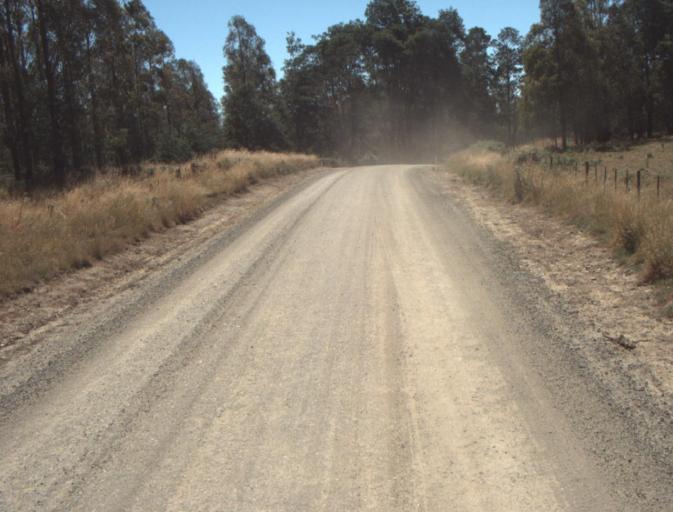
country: AU
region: Tasmania
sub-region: Dorset
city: Scottsdale
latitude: -41.3346
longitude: 147.4336
